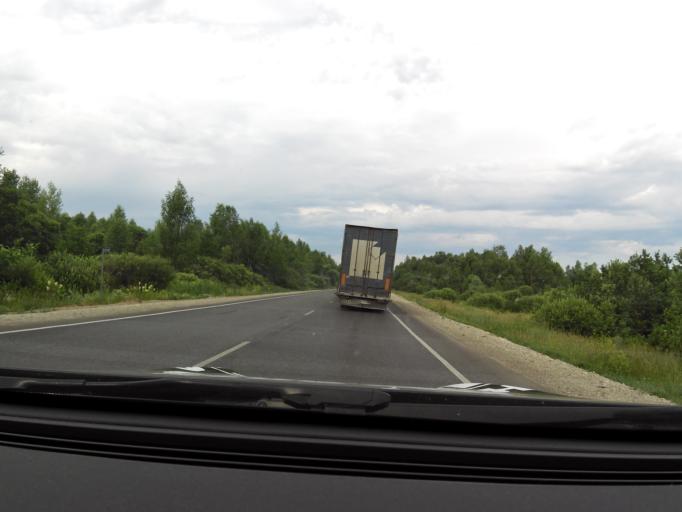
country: RU
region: Bashkortostan
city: Ulu-Telyak
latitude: 54.8473
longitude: 57.1032
